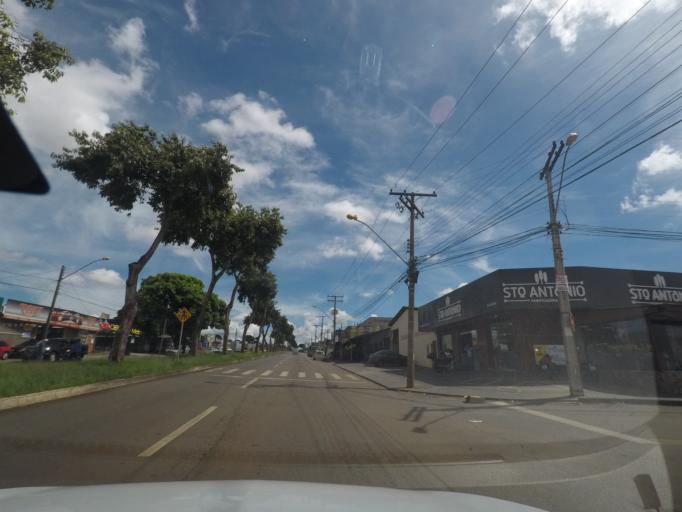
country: BR
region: Goias
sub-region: Goiania
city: Goiania
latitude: -16.7336
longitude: -49.3260
